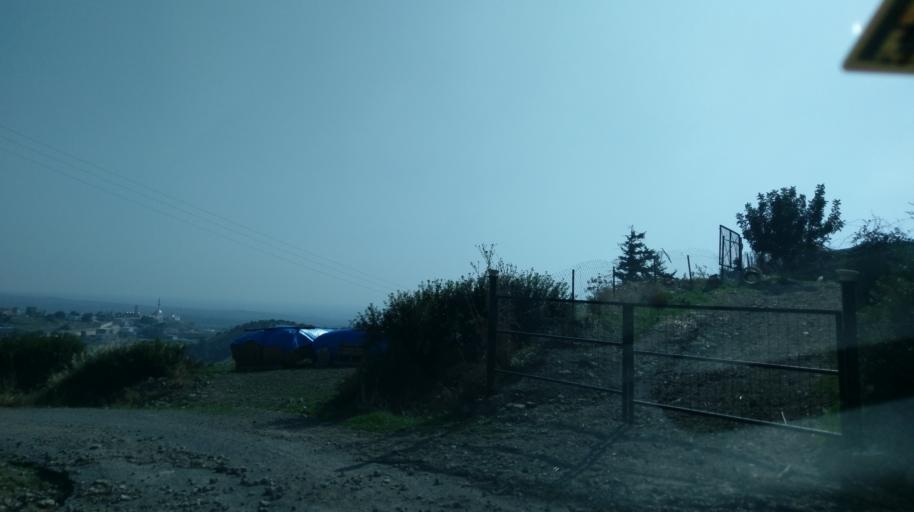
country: CY
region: Ammochostos
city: Lefkonoiko
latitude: 35.3126
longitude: 33.6252
